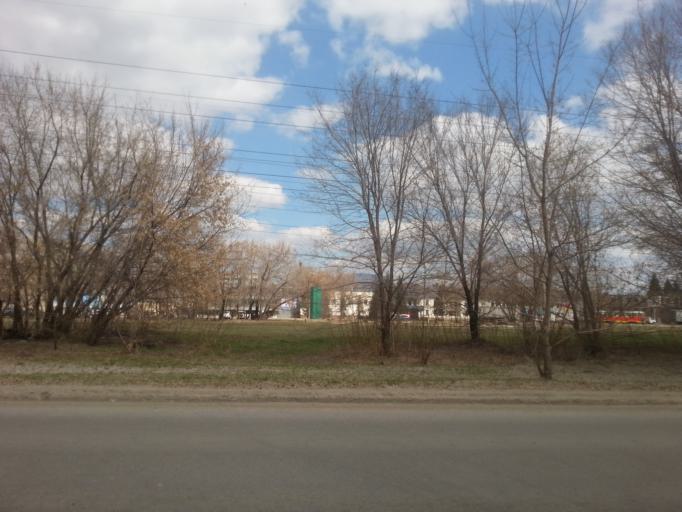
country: RU
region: Altai Krai
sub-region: Gorod Barnaulskiy
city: Barnaul
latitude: 53.3860
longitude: 83.7223
